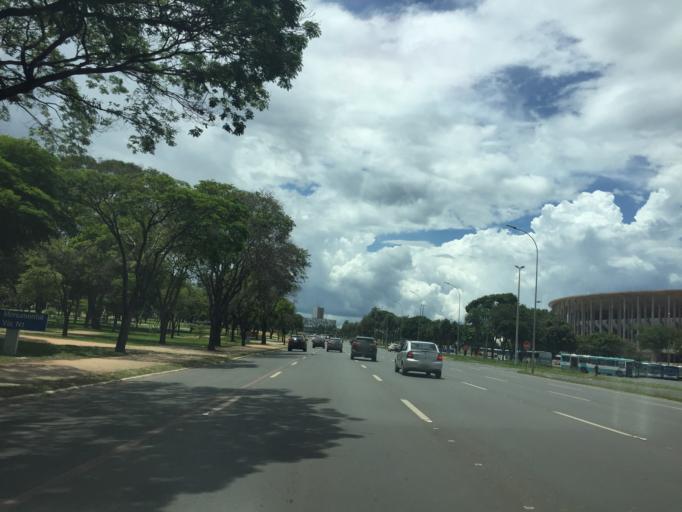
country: BR
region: Federal District
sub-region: Brasilia
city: Brasilia
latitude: -15.7878
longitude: -47.8961
